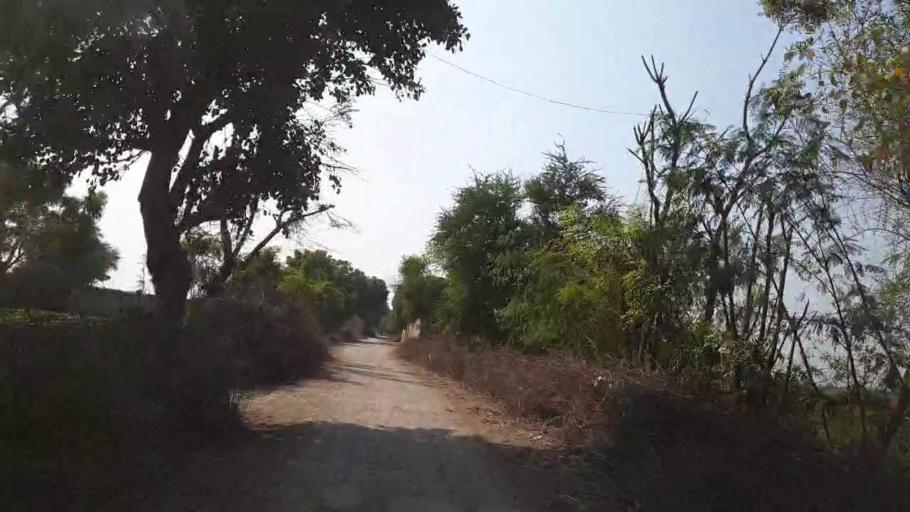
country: PK
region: Sindh
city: Bhit Shah
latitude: 25.7518
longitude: 68.4671
